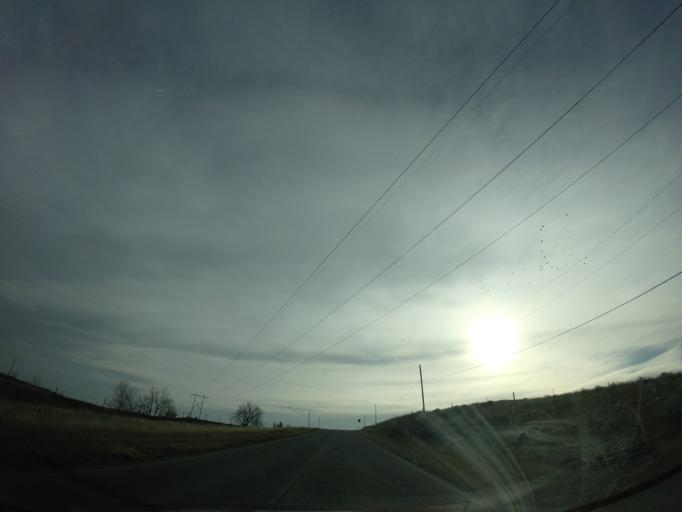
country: US
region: Montana
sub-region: Yellowstone County
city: Billings
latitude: 45.7928
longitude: -108.4555
